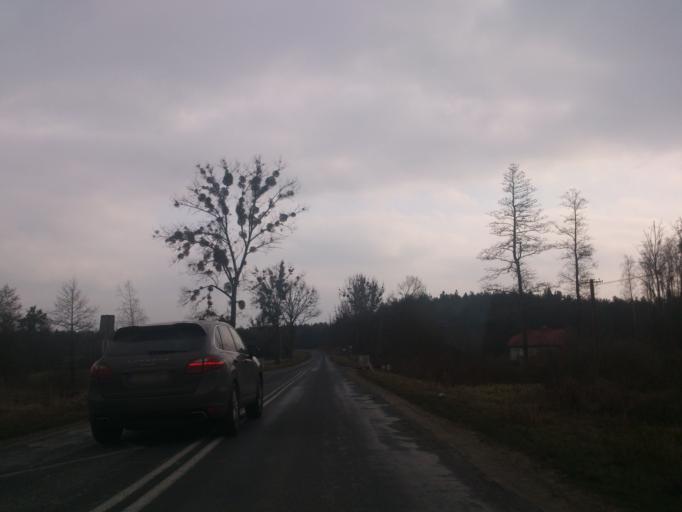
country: PL
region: Kujawsko-Pomorskie
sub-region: Powiat golubsko-dobrzynski
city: Golub-Dobrzyn
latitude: 53.0931
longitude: 19.0483
